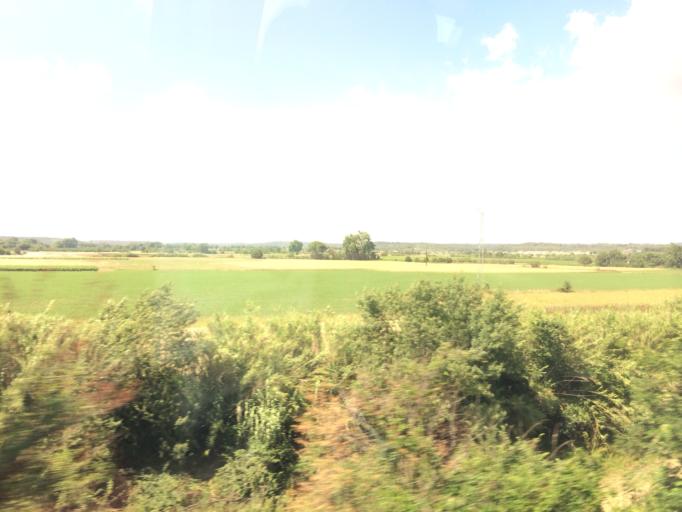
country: FR
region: Languedoc-Roussillon
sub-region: Departement du Gard
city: Gallargues-le-Montueux
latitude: 43.7100
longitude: 4.1624
